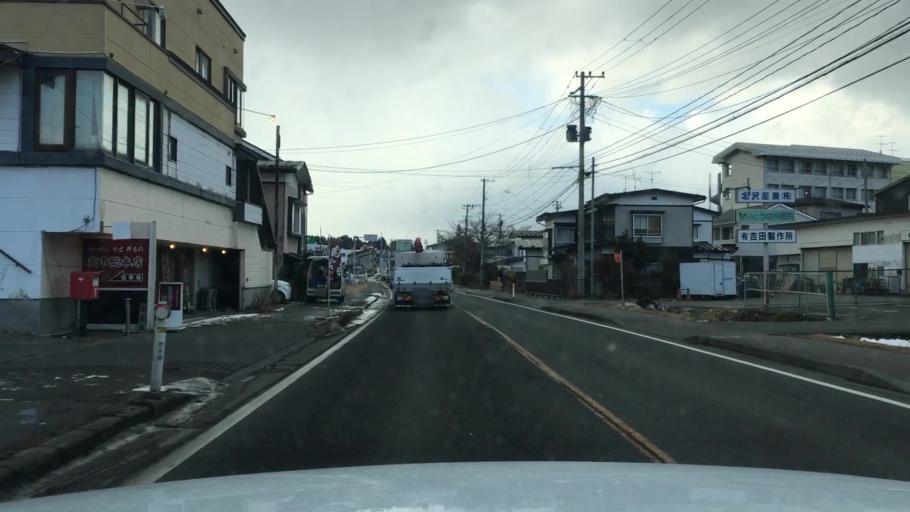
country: JP
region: Iwate
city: Morioka-shi
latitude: 39.6897
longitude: 141.1757
